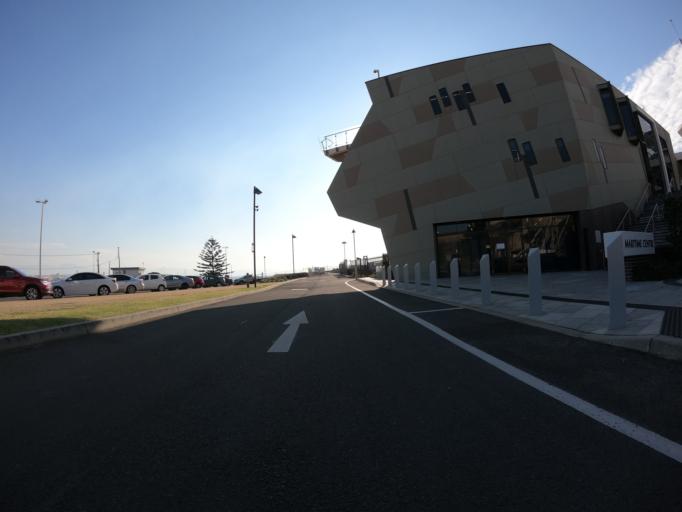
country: AU
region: New South Wales
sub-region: Wollongong
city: Port Kembla
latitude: -34.4755
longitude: 150.9126
